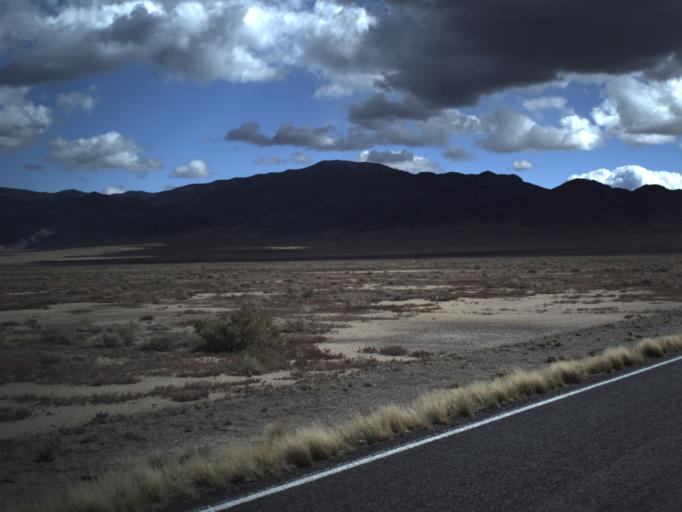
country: US
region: Utah
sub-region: Beaver County
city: Milford
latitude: 38.5276
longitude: -113.6691
